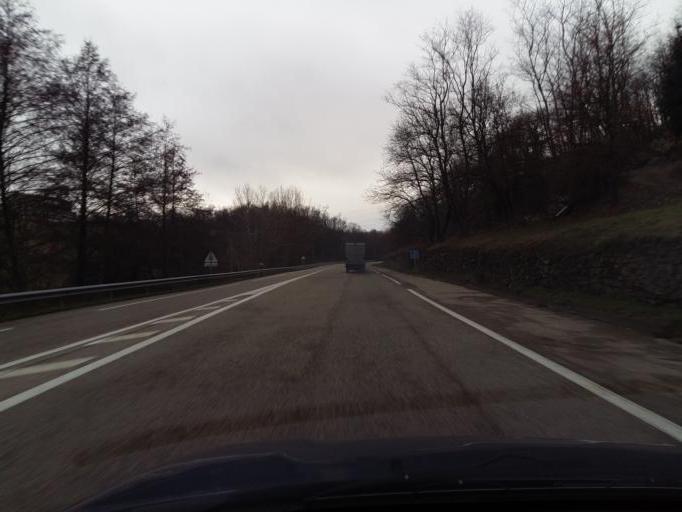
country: FR
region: Rhone-Alpes
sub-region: Departement de l'Ardeche
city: Saint-Cyr
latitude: 45.2512
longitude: 4.7551
